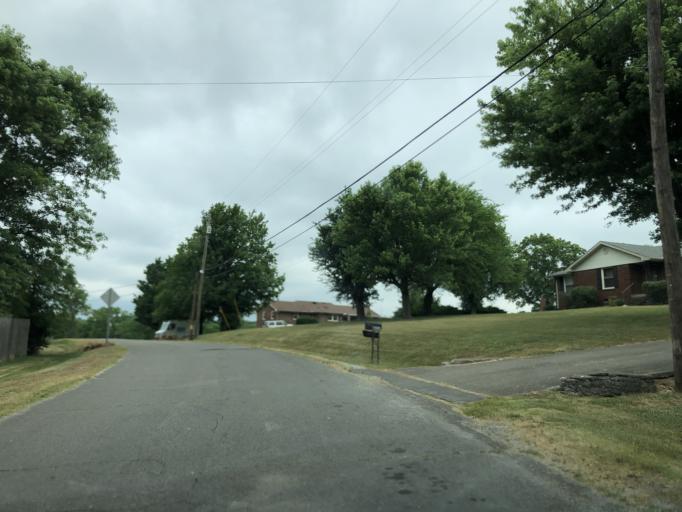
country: US
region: Tennessee
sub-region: Davidson County
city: Goodlettsville
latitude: 36.2799
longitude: -86.7628
